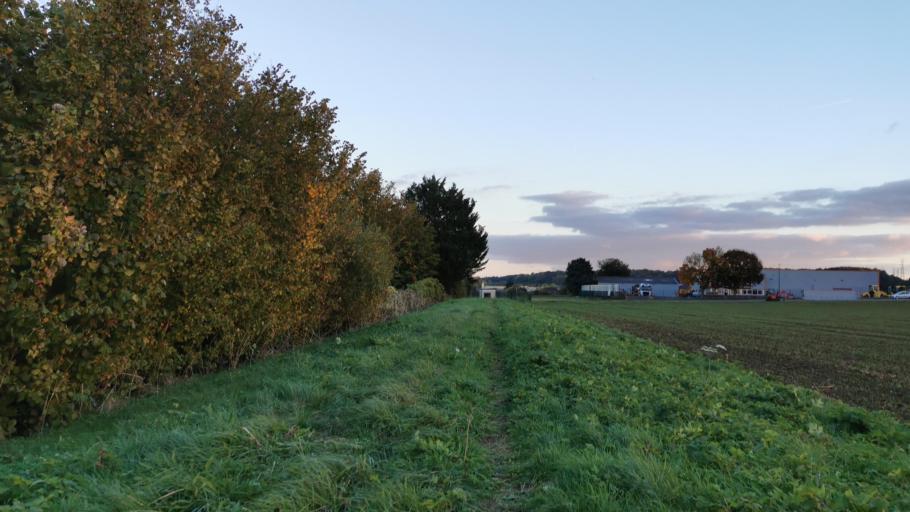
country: FR
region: Ile-de-France
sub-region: Departement des Yvelines
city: Plaisir
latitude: 48.8232
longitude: 1.9367
